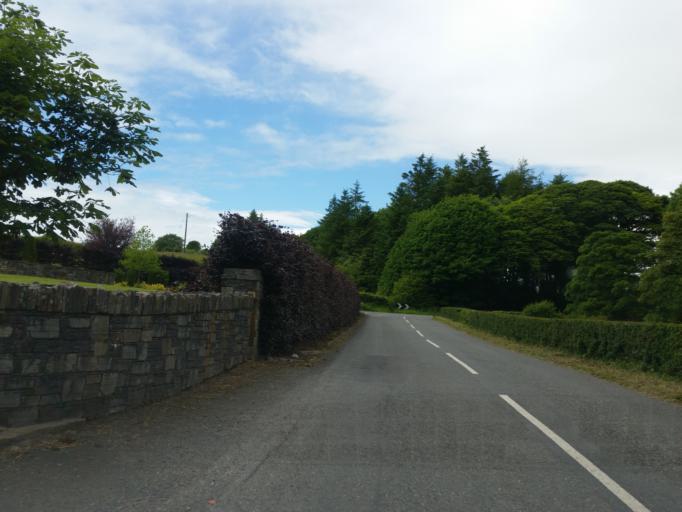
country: GB
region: Northern Ireland
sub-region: Omagh District
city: Omagh
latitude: 54.5200
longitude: -7.0772
